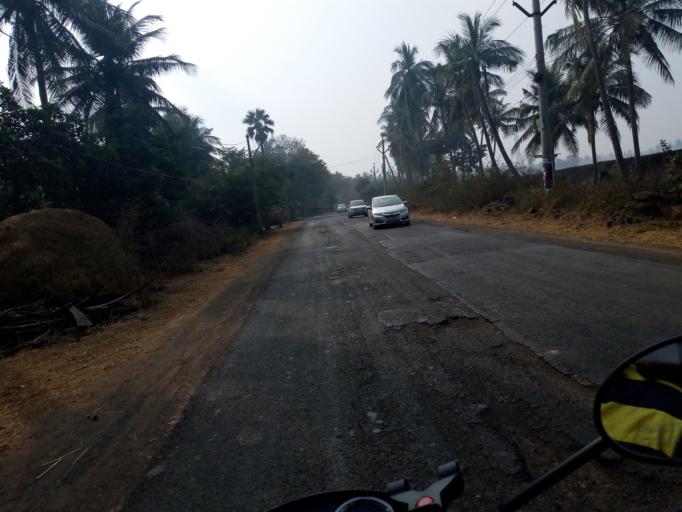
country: IN
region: Andhra Pradesh
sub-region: West Godavari
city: Pippara
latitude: 16.7325
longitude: 81.4194
